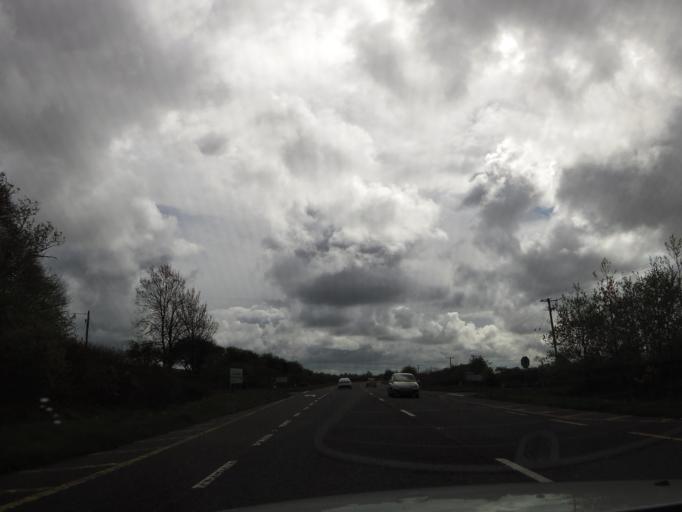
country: IE
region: Connaught
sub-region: Maigh Eo
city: Claremorris
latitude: 53.7442
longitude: -8.9682
